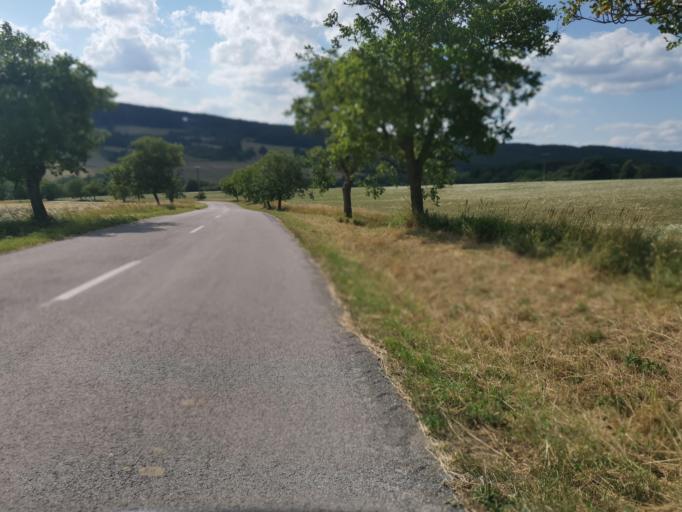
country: CZ
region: South Moravian
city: Knezdub
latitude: 48.8051
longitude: 17.4216
